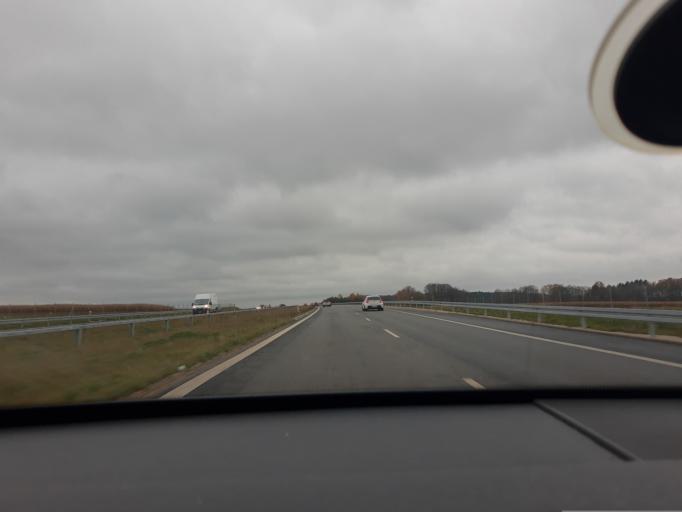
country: PL
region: Lodz Voivodeship
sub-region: Powiat pabianicki
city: Konstantynow Lodzki
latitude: 51.7114
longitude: 19.3459
